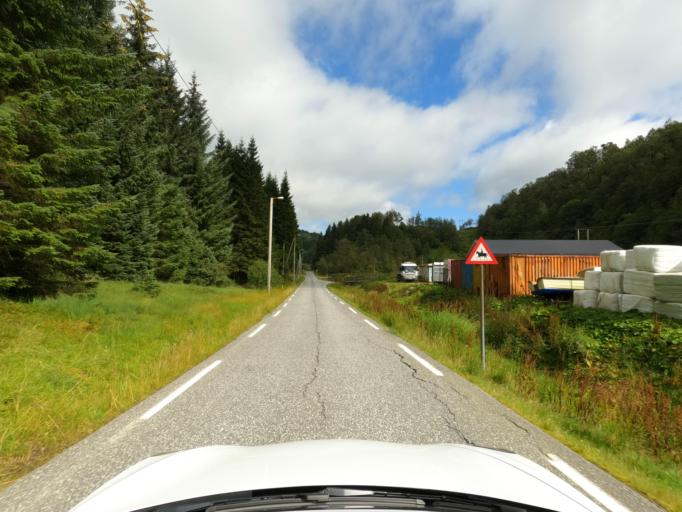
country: NO
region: Hordaland
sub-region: Bergen
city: Espeland
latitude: 60.3135
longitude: 5.4712
